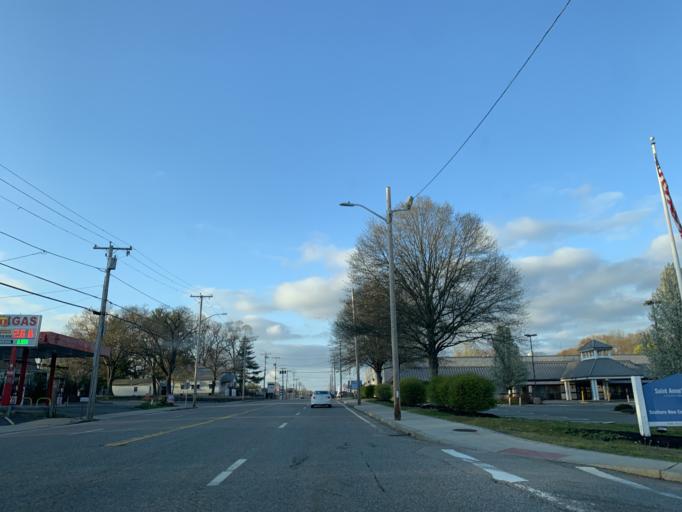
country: US
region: Rhode Island
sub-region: Providence County
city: Valley Falls
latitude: 41.9063
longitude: -71.3651
